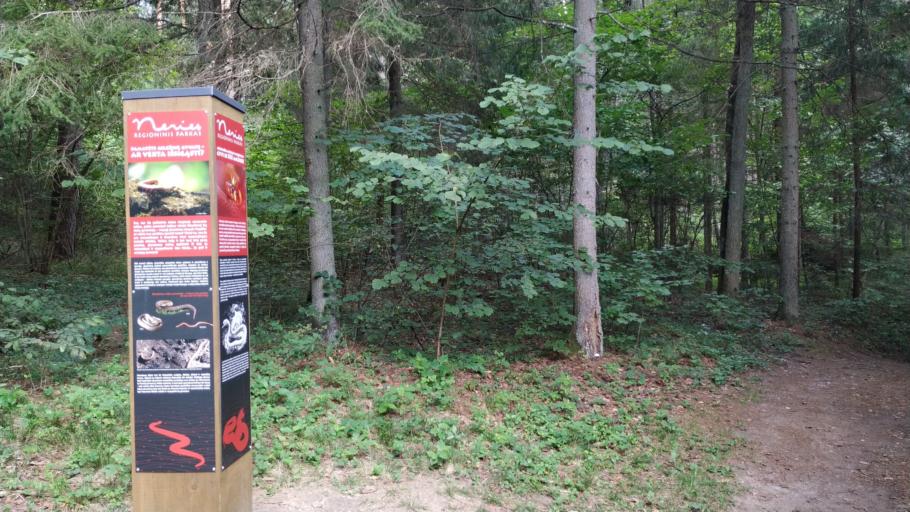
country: LT
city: Grigiskes
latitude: 54.8095
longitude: 24.9756
